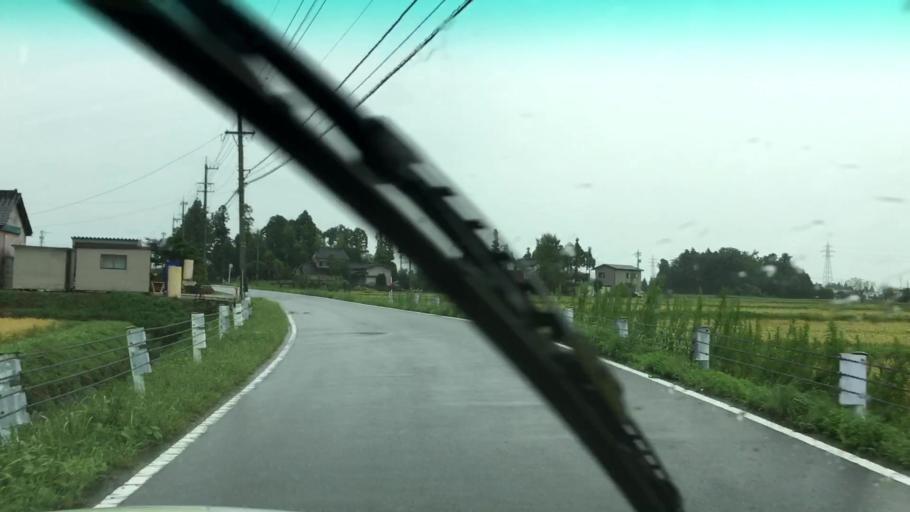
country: JP
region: Toyama
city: Kamiichi
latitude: 36.6751
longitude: 137.3211
